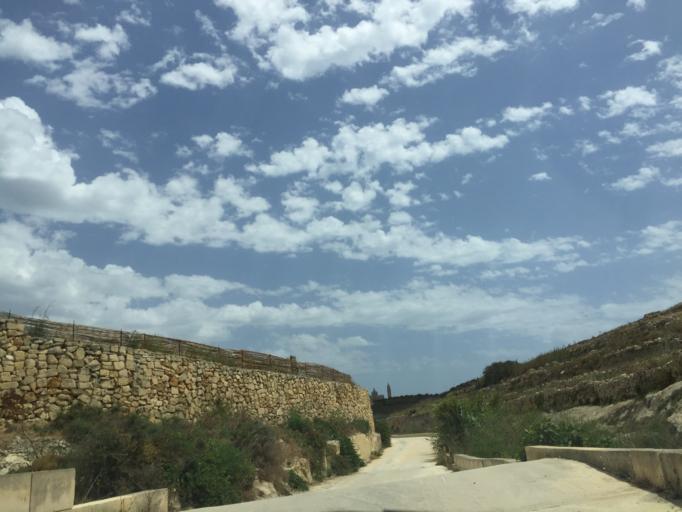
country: MT
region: L-Gharb
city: Gharb
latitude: 36.0711
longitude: 14.2093
